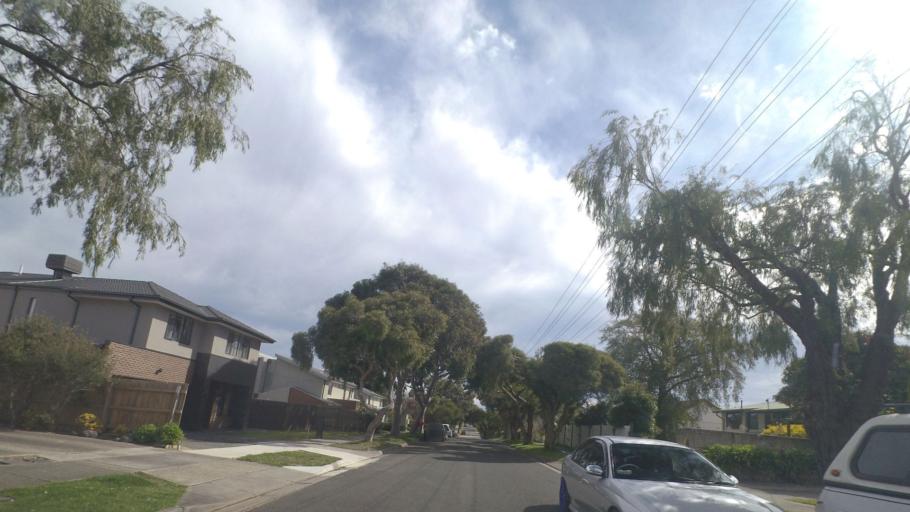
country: AU
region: Victoria
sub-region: Knox
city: Bayswater
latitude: -37.8496
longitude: 145.2622
